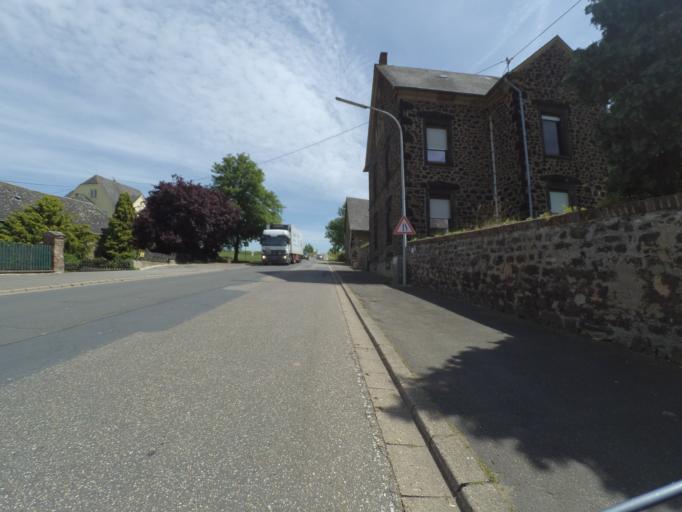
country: DE
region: Rheinland-Pfalz
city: Kerben
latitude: 50.3149
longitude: 7.3766
